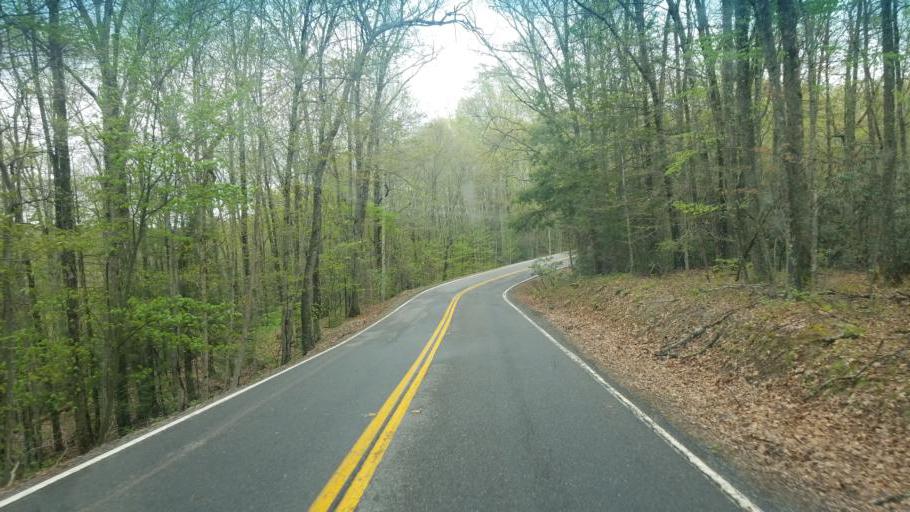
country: US
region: Virginia
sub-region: Tazewell County
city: Tazewell
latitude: 36.9896
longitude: -81.5306
